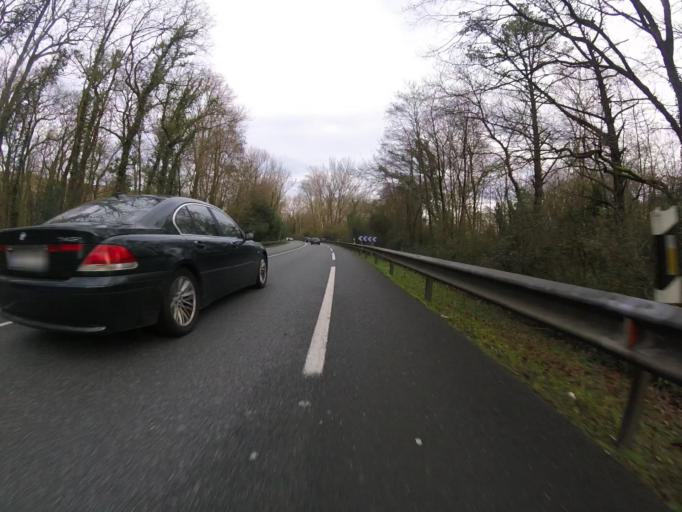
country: ES
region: Basque Country
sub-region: Provincia de Guipuzcoa
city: Irun
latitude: 43.3339
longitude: -1.8219
